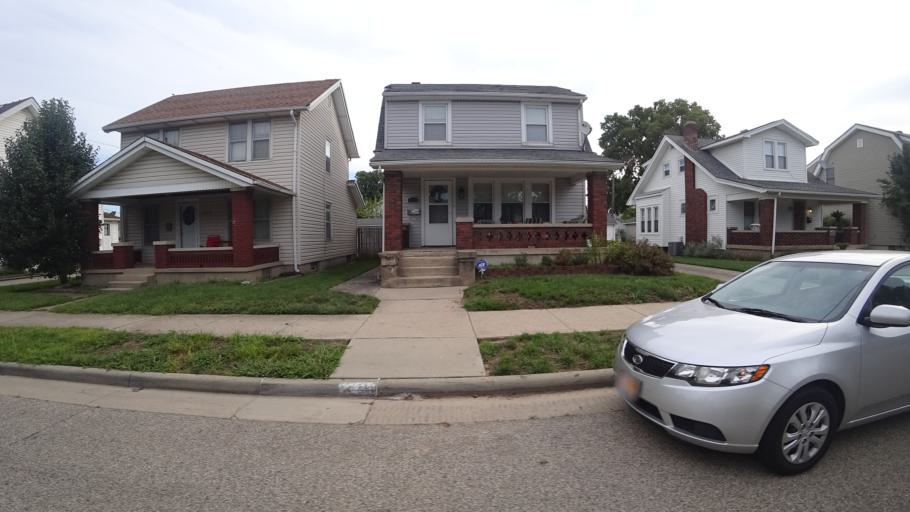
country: US
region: Ohio
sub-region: Butler County
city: Hamilton
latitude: 39.3939
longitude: -84.5444
